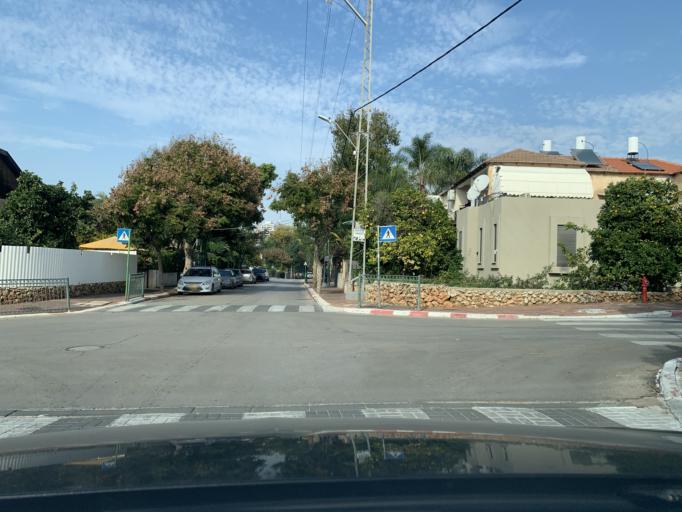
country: IL
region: Tel Aviv
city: Giv`at Shemu'el
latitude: 32.0632
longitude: 34.8538
